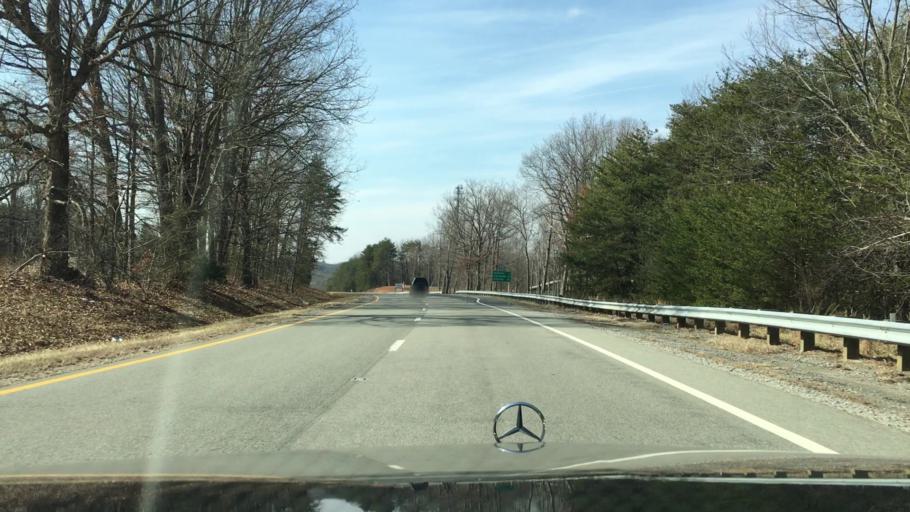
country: US
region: Virginia
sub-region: Prince Edward County
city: Hampden Sydney
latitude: 37.3162
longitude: -78.4720
